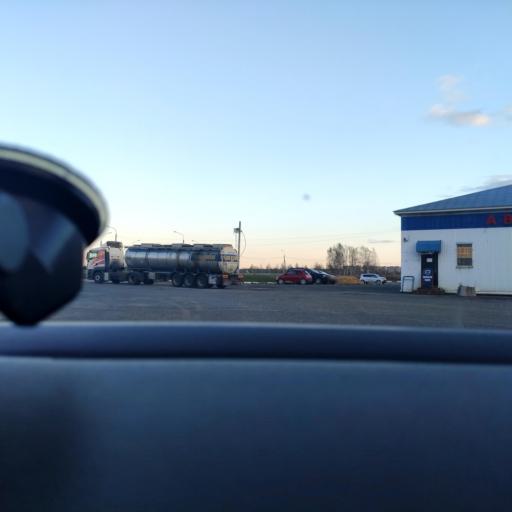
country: RU
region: Moskovskaya
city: Yegor'yevsk
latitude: 55.3891
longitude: 39.0775
